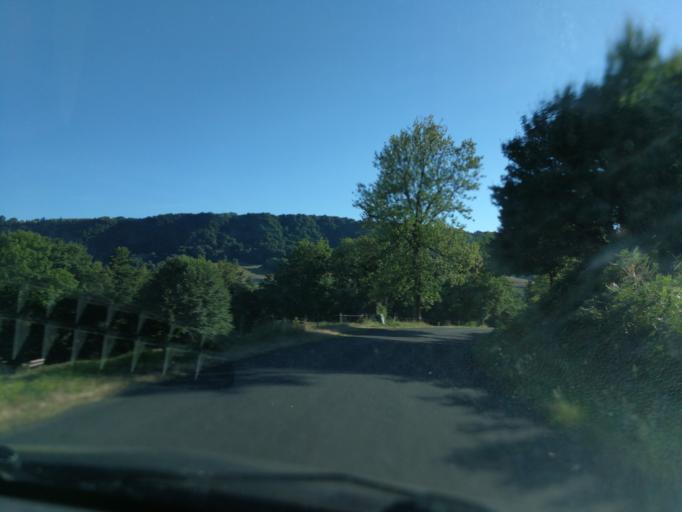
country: FR
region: Auvergne
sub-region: Departement du Cantal
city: Saint-Cernin
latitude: 45.1286
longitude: 2.4952
